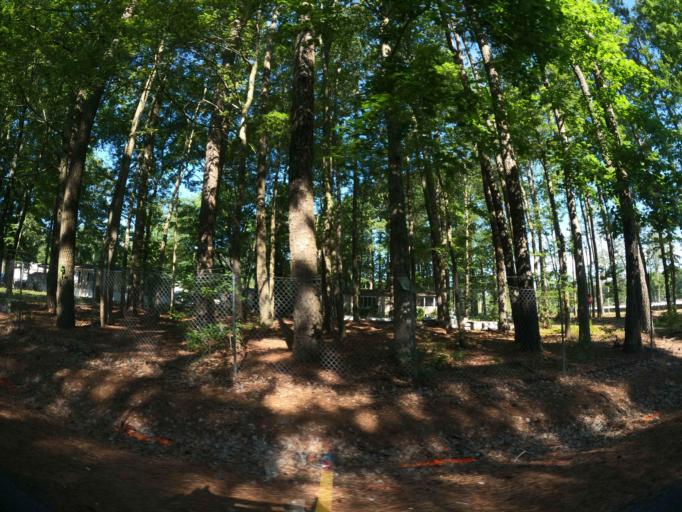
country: US
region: Delaware
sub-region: Sussex County
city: Ocean View
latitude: 38.5194
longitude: -75.0978
